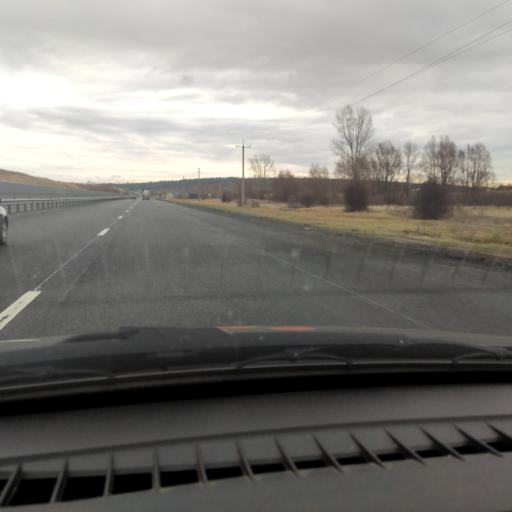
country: RU
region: Samara
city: Kurumoch
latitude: 53.4996
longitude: 50.0251
